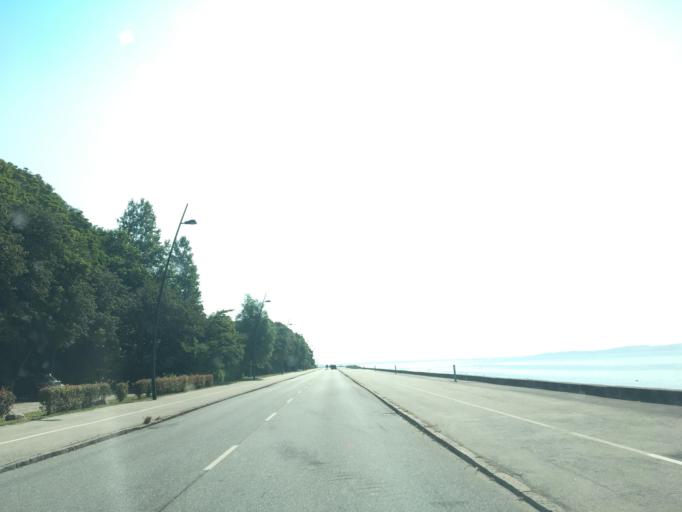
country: DK
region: North Denmark
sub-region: Thisted Kommune
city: Thisted
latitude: 56.9520
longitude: 8.6819
